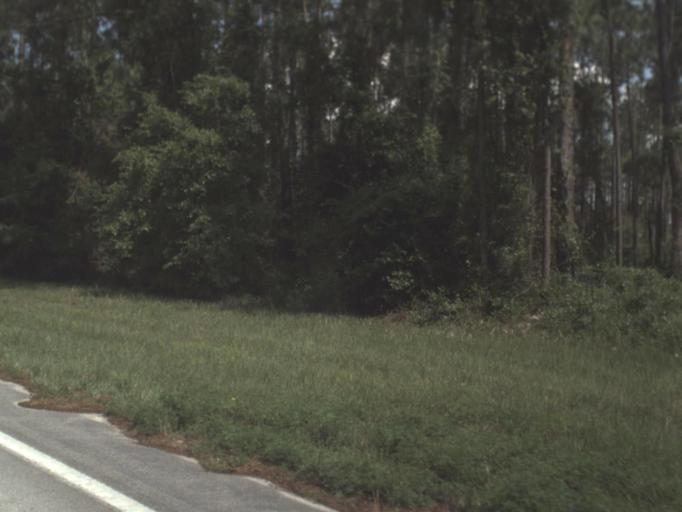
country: US
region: Florida
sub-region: Bradford County
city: Starke
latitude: 29.9385
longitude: -82.0284
